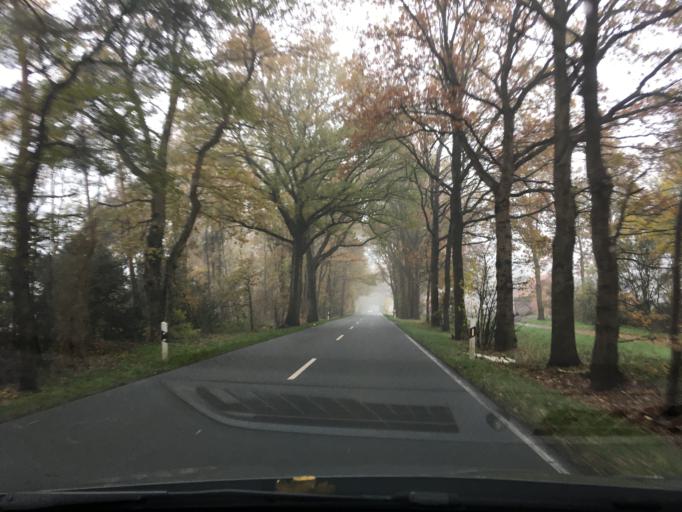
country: DE
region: North Rhine-Westphalia
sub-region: Regierungsbezirk Munster
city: Ahaus
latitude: 52.1094
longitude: 6.9175
